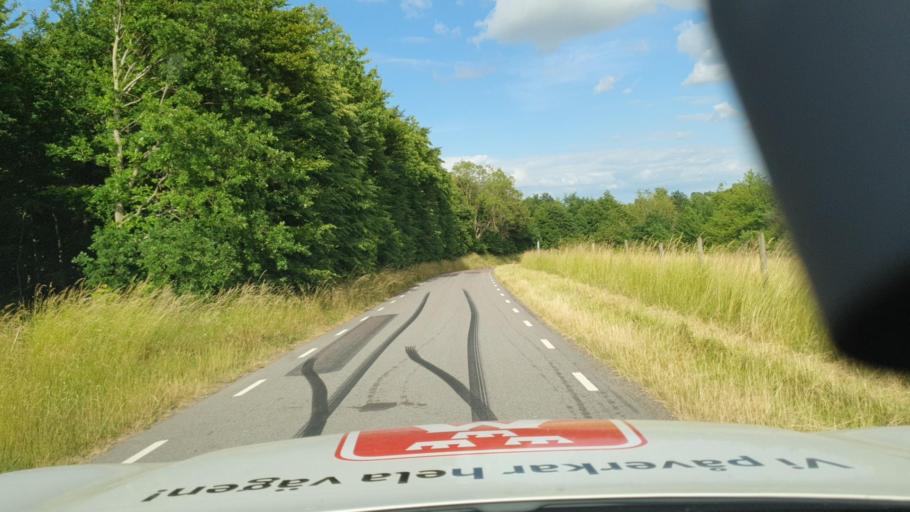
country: SE
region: Skane
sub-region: Skurups Kommun
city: Skurup
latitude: 55.4541
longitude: 13.5320
